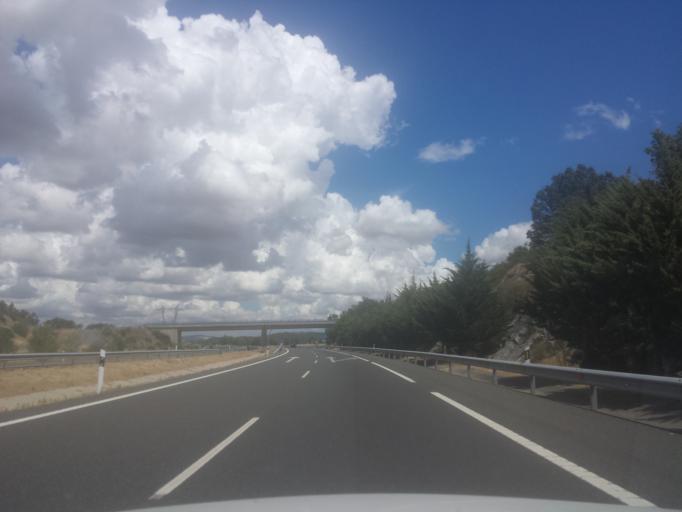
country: ES
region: Castille and Leon
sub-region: Provincia de Salamanca
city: Cantagallo
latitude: 40.3718
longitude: -5.8253
